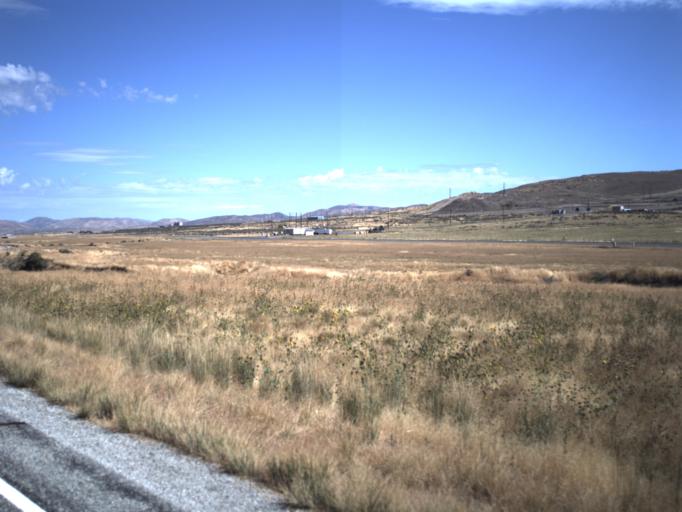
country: US
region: Utah
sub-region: Box Elder County
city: Tremonton
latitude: 41.6799
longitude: -112.4441
